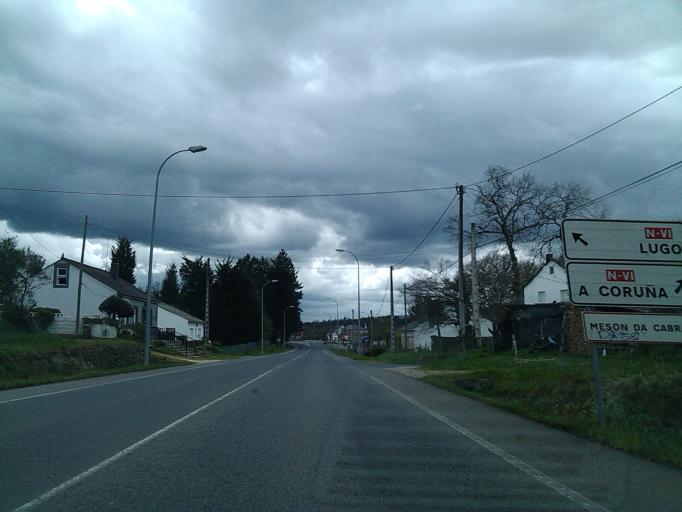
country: ES
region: Galicia
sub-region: Provincia de Lugo
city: Guitiriz
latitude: 43.1808
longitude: -7.8275
